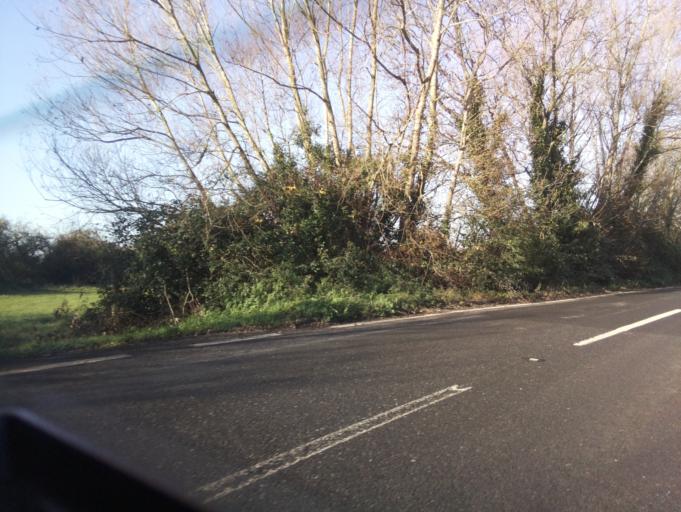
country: GB
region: England
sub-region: Somerset
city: Langport
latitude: 51.0766
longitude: -2.8552
